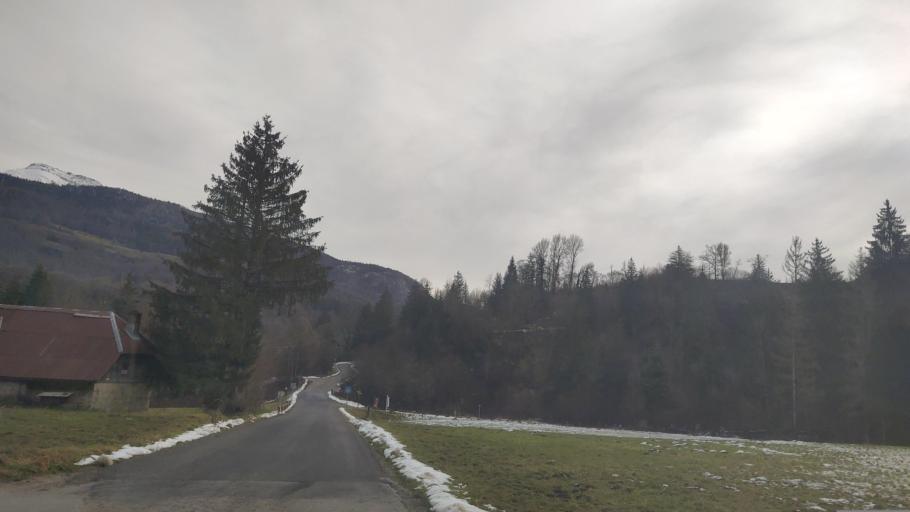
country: FR
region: Rhone-Alpes
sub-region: Departement de la Haute-Savoie
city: Gruffy
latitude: 45.6889
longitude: 6.1159
